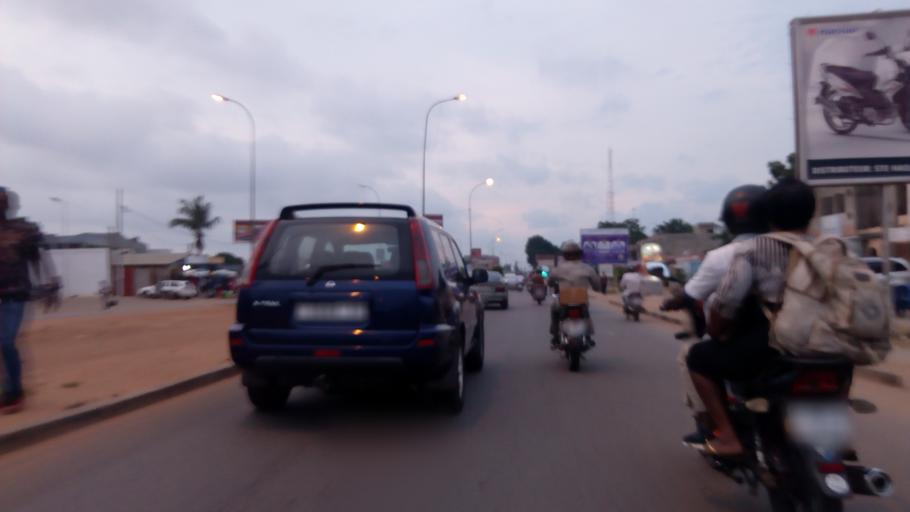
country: TG
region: Maritime
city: Lome
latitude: 6.1992
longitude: 1.1797
